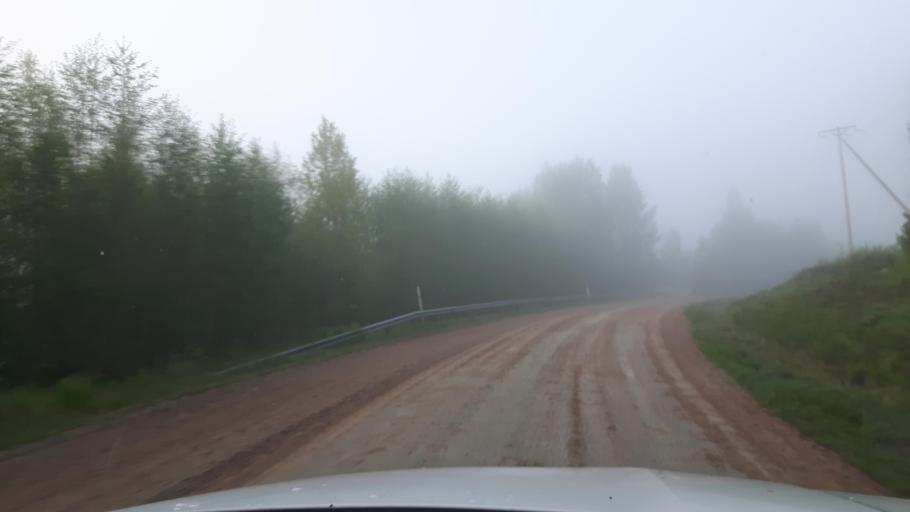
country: SE
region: Vaesternorrland
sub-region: Ange Kommun
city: Ange
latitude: 62.1552
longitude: 15.6634
